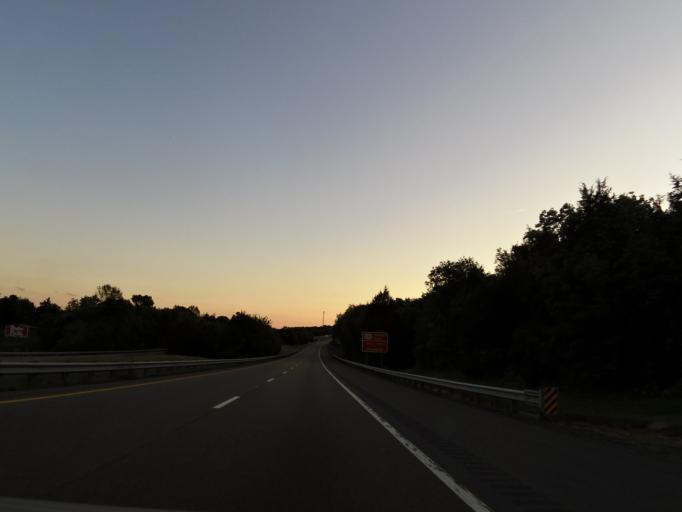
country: US
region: Tennessee
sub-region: Jefferson County
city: White Pine
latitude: 36.1484
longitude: -83.2507
